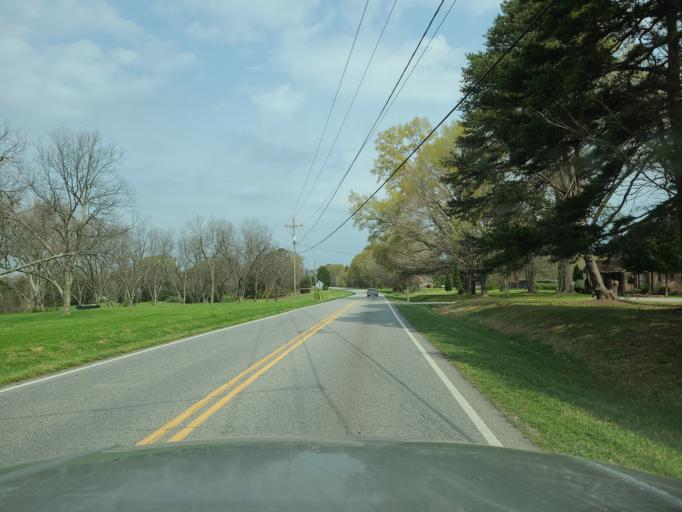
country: US
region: North Carolina
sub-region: Gaston County
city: Stanley
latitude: 35.3376
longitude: -81.0919
